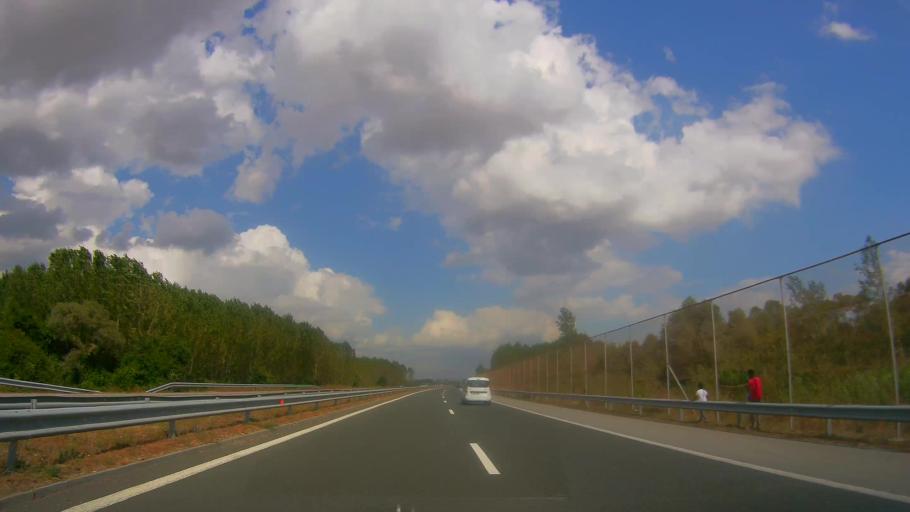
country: BG
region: Yambol
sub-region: Obshtina Yambol
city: Yambol
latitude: 42.5493
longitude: 26.4978
